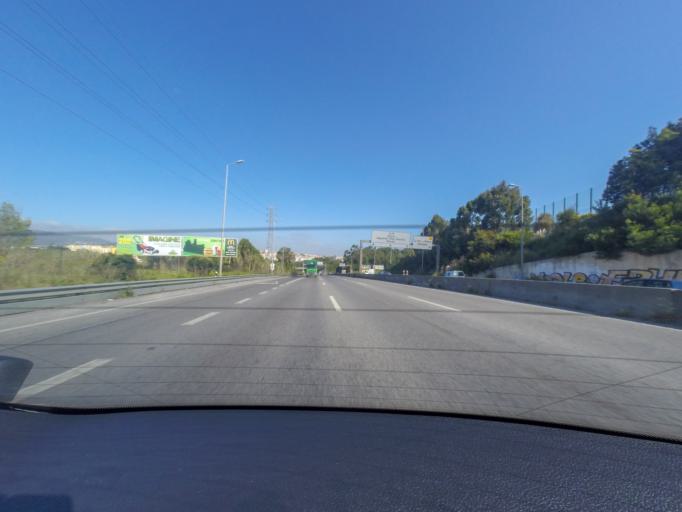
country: PT
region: Lisbon
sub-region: Sintra
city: Rio de Mouro
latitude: 38.7746
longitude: -9.3210
